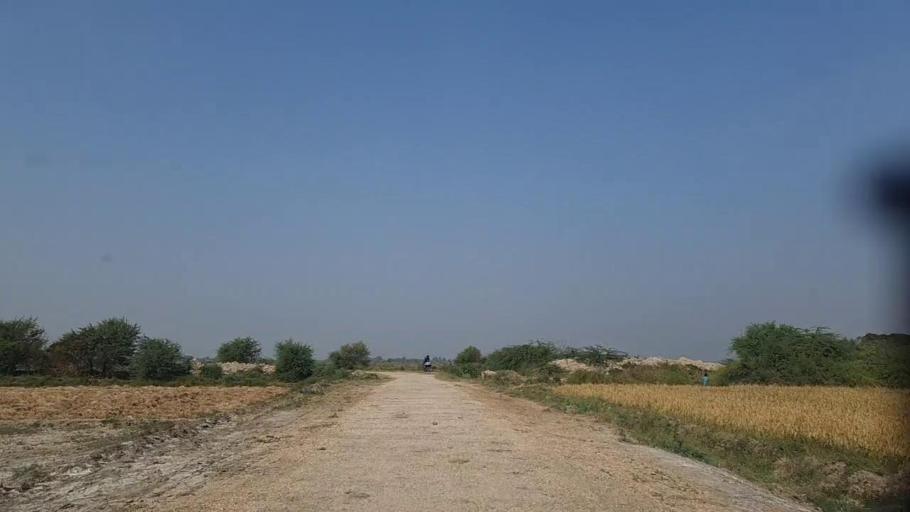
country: PK
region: Sindh
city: Mirpur Batoro
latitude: 24.5854
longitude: 68.1364
